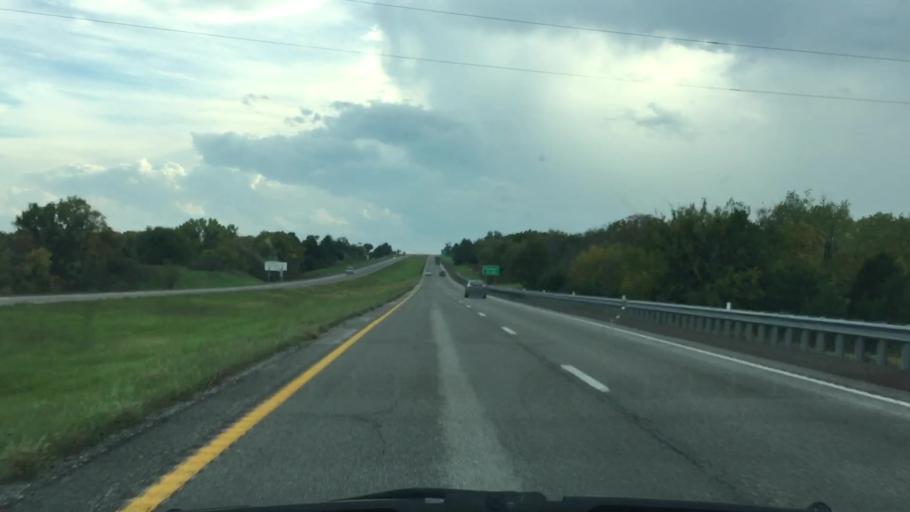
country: US
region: Missouri
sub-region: Clinton County
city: Cameron
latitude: 39.8676
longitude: -94.1707
